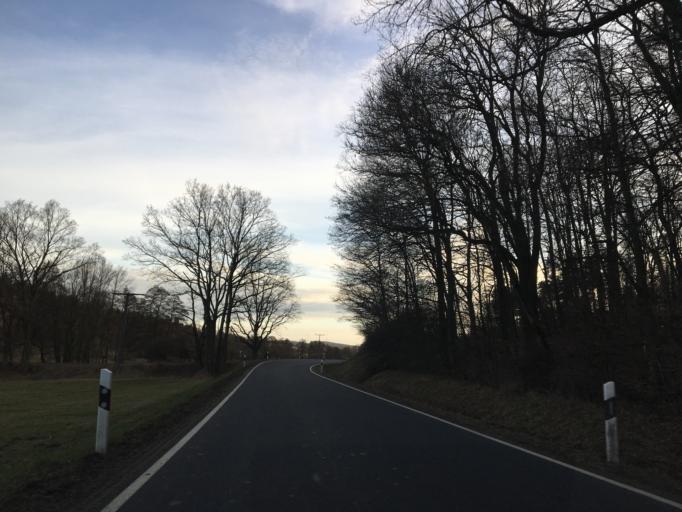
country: DE
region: Hesse
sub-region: Regierungsbezirk Giessen
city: Schwalmtal
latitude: 50.6783
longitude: 9.2828
